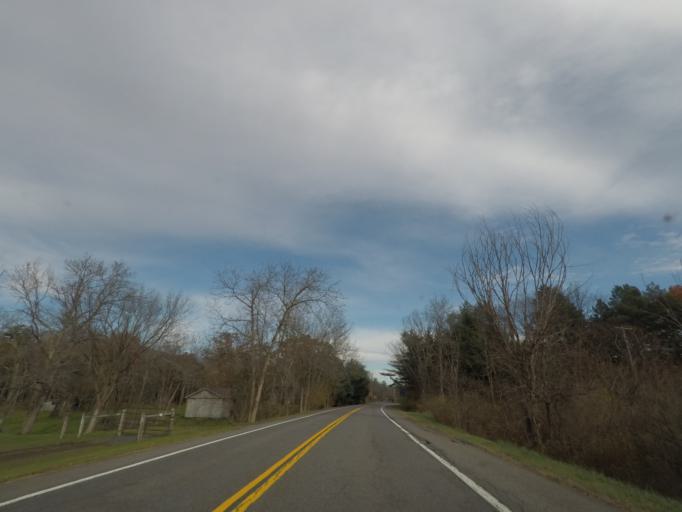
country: US
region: New York
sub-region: Albany County
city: Voorheesville
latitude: 42.6453
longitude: -73.9526
